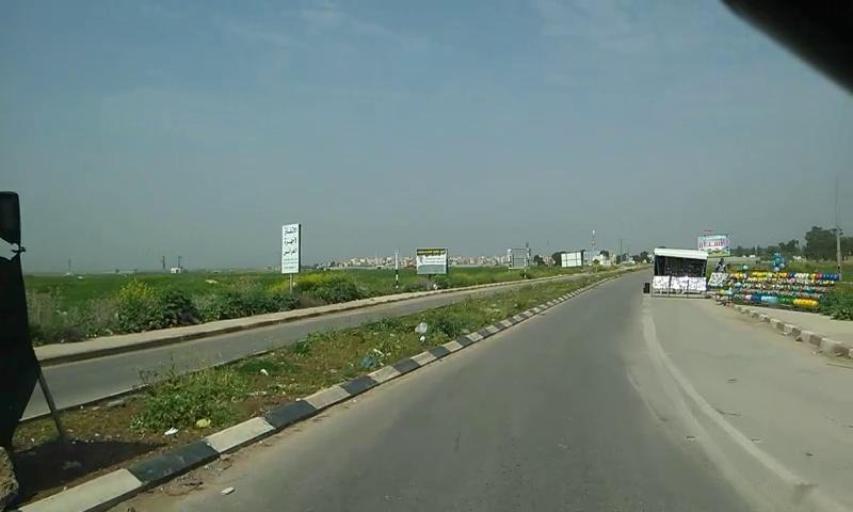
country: PS
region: West Bank
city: Al Jalamah
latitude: 32.5002
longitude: 35.3020
